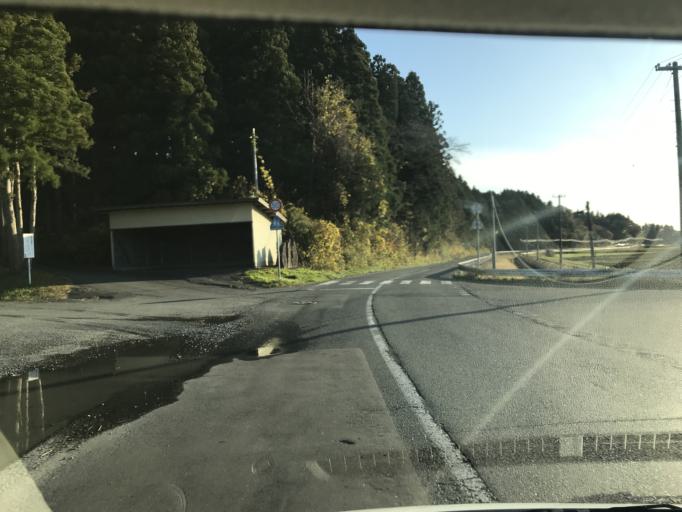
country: JP
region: Iwate
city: Mizusawa
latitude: 39.0663
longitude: 141.1836
